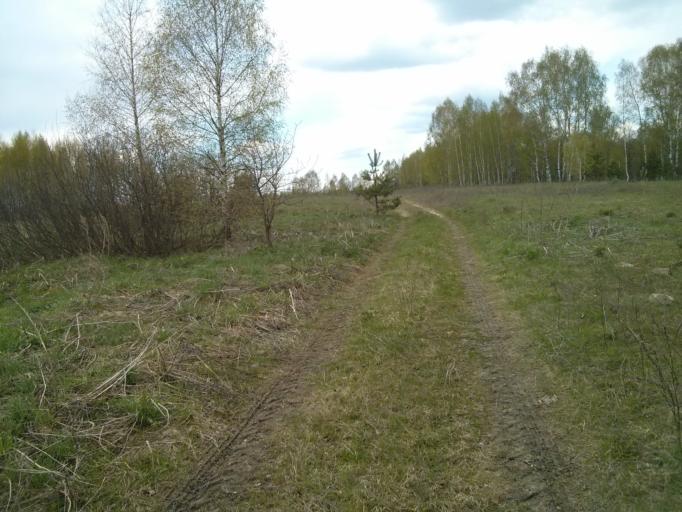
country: RU
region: Nizjnij Novgorod
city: Shimorskoye
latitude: 55.3084
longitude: 41.8504
